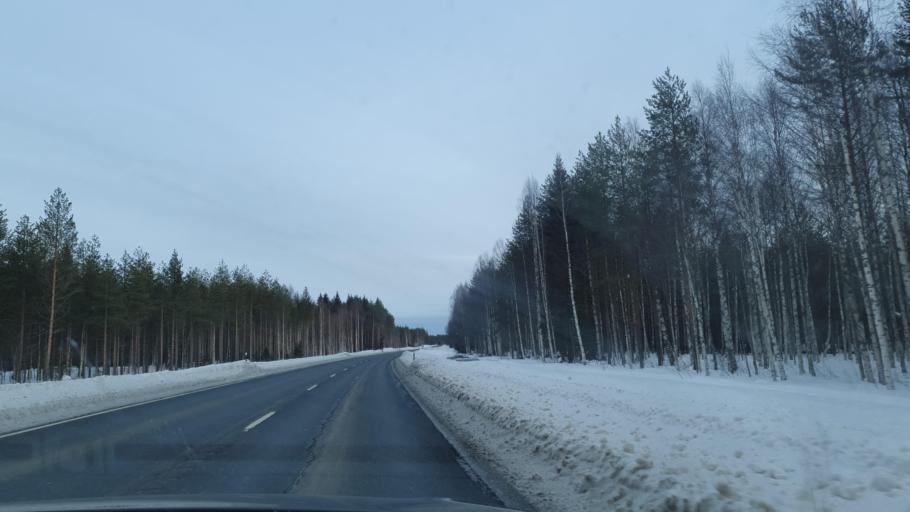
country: FI
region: Kainuu
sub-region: Kehys-Kainuu
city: Kuhmo
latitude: 64.1051
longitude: 29.3189
